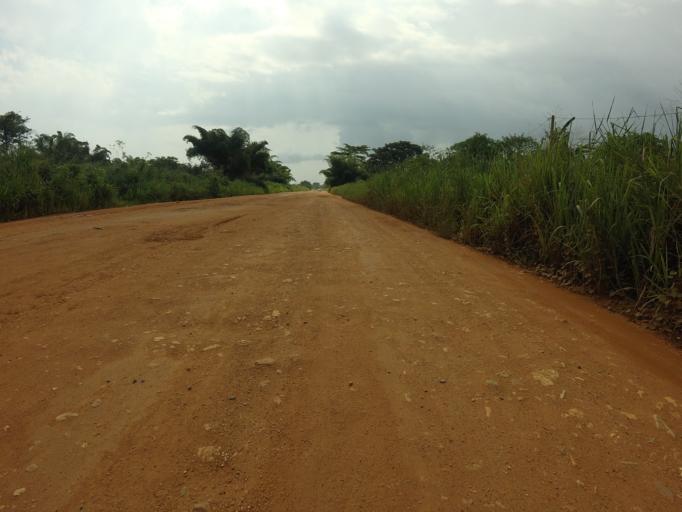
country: GH
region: Volta
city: Kpandu
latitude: 6.9861
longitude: 0.4454
